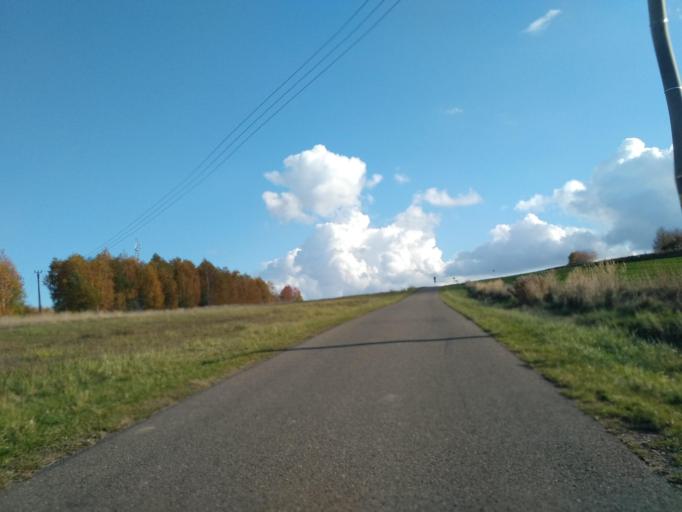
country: PL
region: Subcarpathian Voivodeship
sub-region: Powiat rzeszowski
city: Zglobien
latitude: 49.9856
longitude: 21.8469
